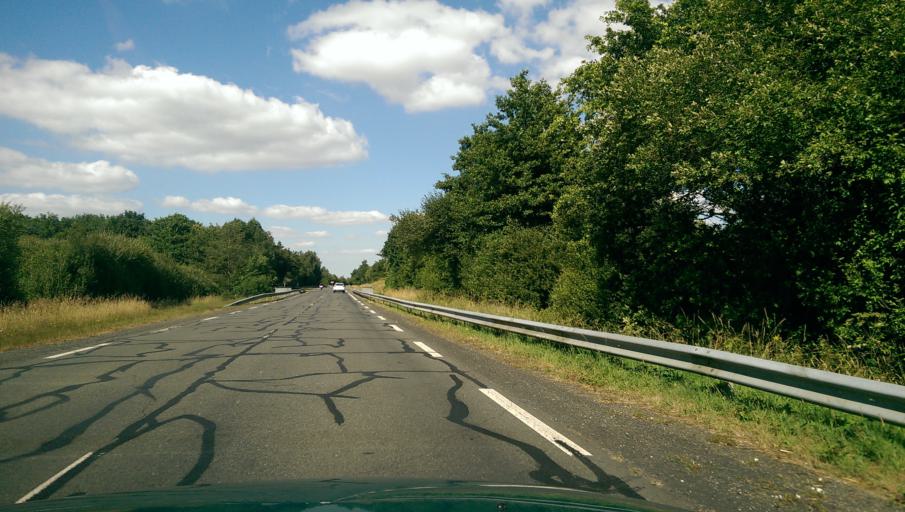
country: FR
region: Pays de la Loire
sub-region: Departement de la Loire-Atlantique
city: Lege
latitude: 46.8871
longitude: -1.6115
